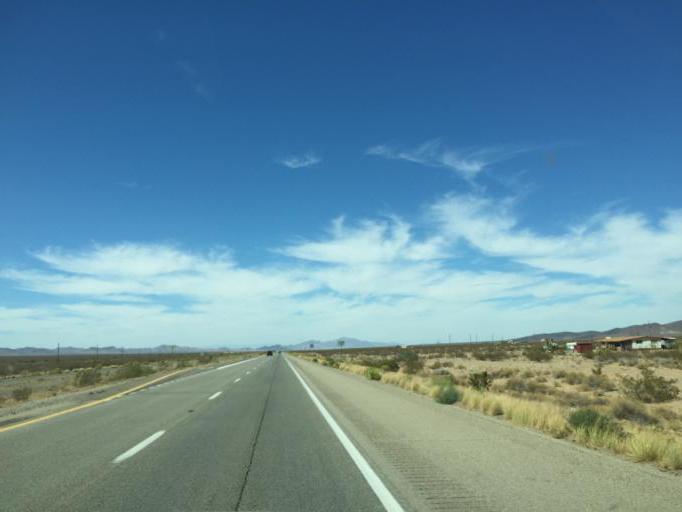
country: US
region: Arizona
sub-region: Mohave County
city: Dolan Springs
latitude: 35.5912
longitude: -114.3949
